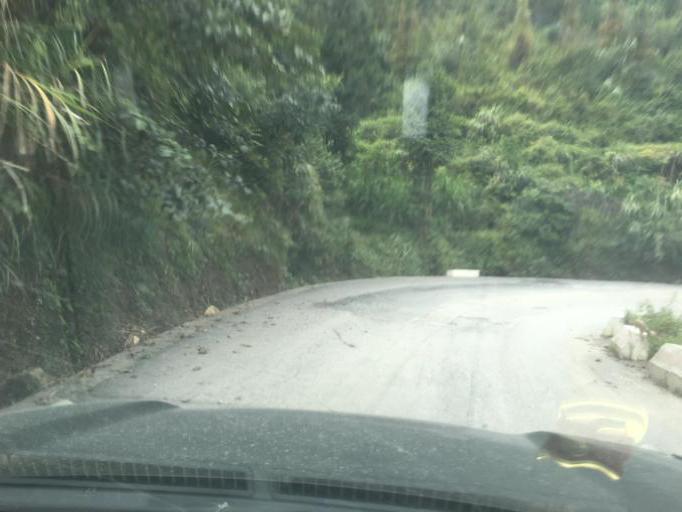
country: CN
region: Guangxi Zhuangzu Zizhiqu
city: Tongle
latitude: 25.3598
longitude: 106.2599
